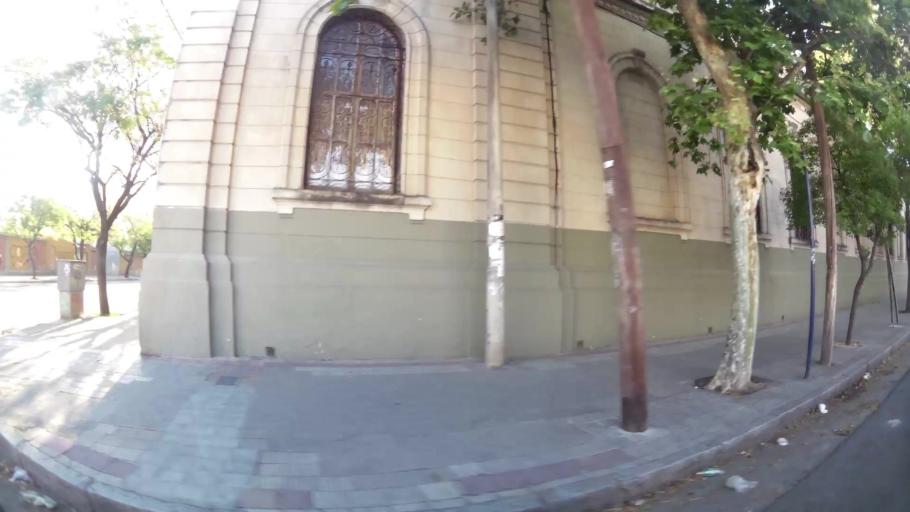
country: AR
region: Cordoba
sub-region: Departamento de Capital
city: Cordoba
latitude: -31.3886
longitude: -64.1839
